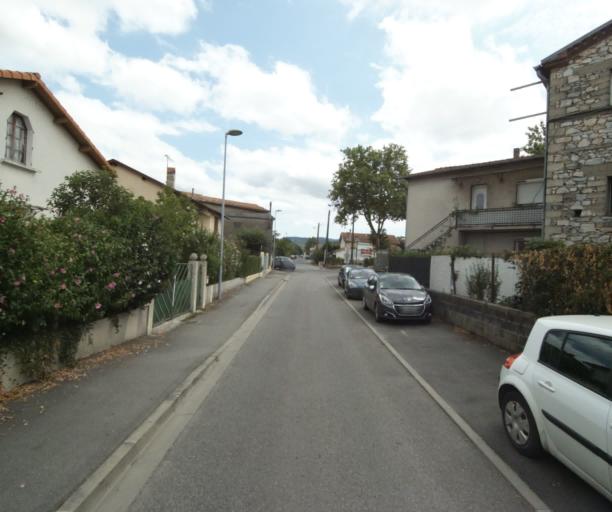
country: FR
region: Midi-Pyrenees
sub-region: Departement de la Haute-Garonne
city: Revel
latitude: 43.4558
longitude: 1.9971
